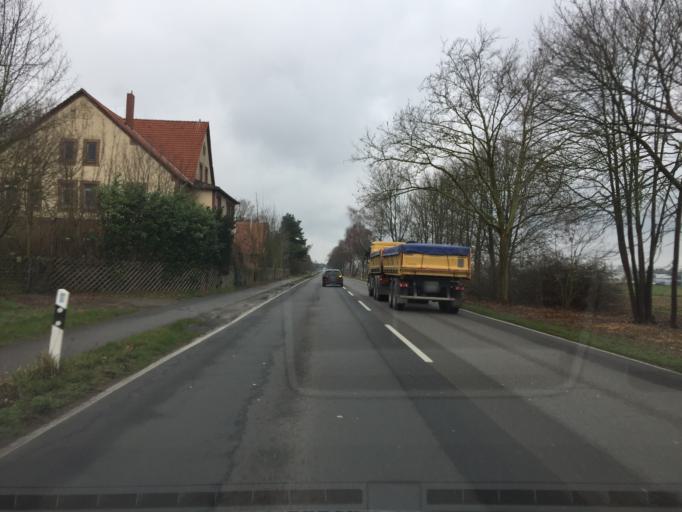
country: DE
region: Lower Saxony
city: Wunstorf
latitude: 52.4060
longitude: 9.4585
